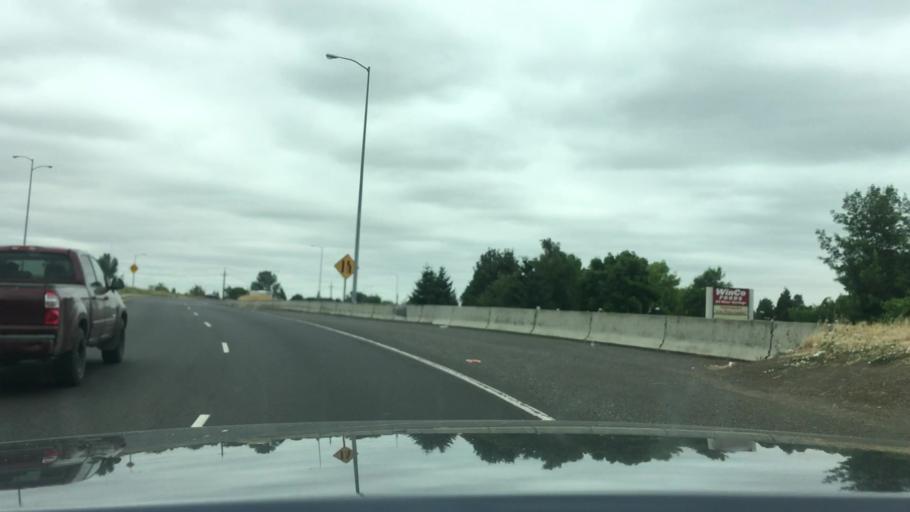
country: US
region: Oregon
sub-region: Lane County
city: Eugene
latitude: 44.0852
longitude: -123.1706
